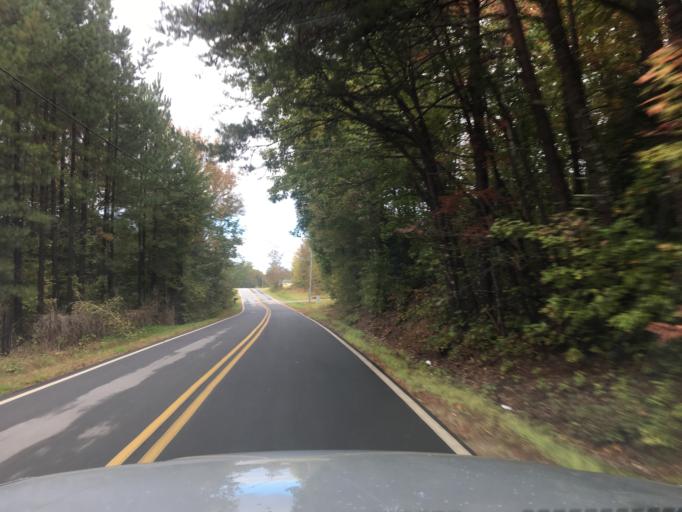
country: US
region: South Carolina
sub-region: Greenville County
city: Tigerville
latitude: 35.0705
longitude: -82.2926
